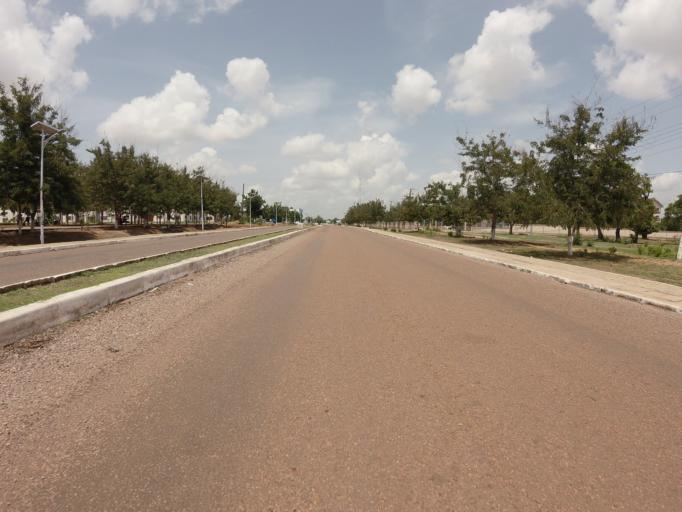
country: GH
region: Northern
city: Tamale
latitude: 9.3713
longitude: -0.8845
